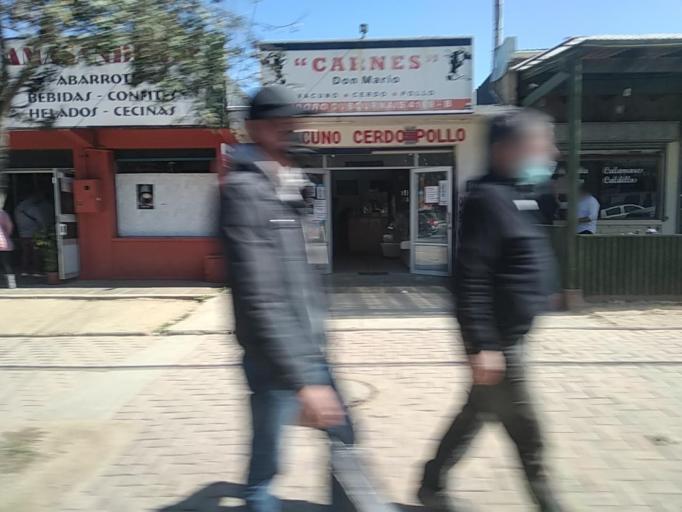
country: CL
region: Valparaiso
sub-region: San Antonio Province
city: El Tabo
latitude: -33.4403
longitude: -71.6834
